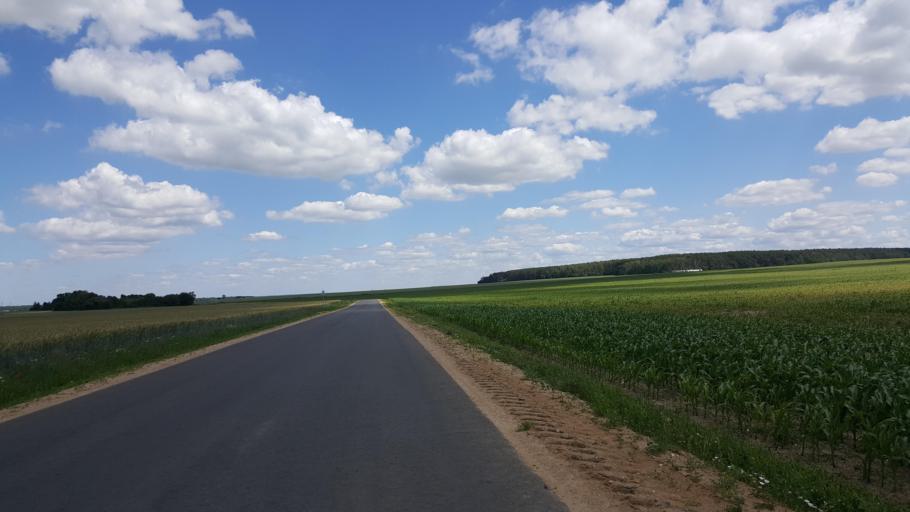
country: BY
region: Brest
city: Vysokaye
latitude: 52.4276
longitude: 23.5260
